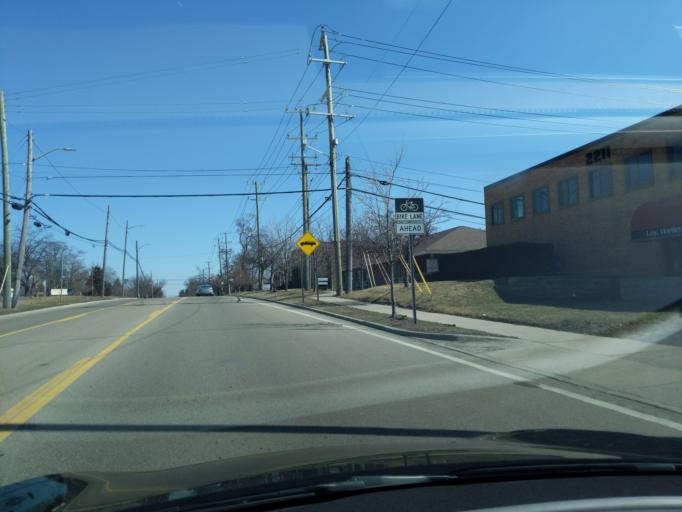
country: US
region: Michigan
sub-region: Washtenaw County
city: Ann Arbor
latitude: 42.2806
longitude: -83.7781
